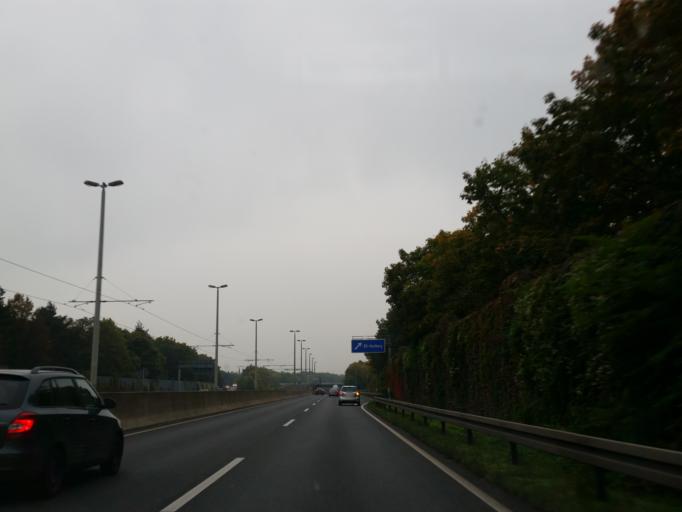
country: DE
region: Lower Saxony
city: Braunschweig
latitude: 52.2319
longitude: 10.5296
